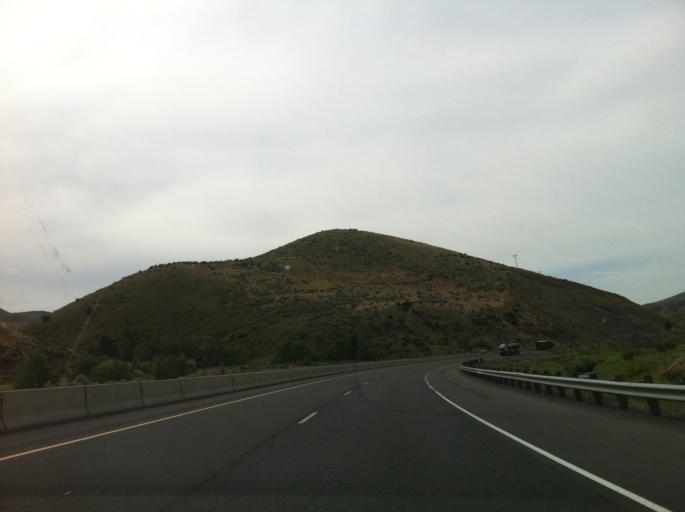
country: US
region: Idaho
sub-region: Washington County
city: Weiser
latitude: 44.4732
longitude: -117.3403
